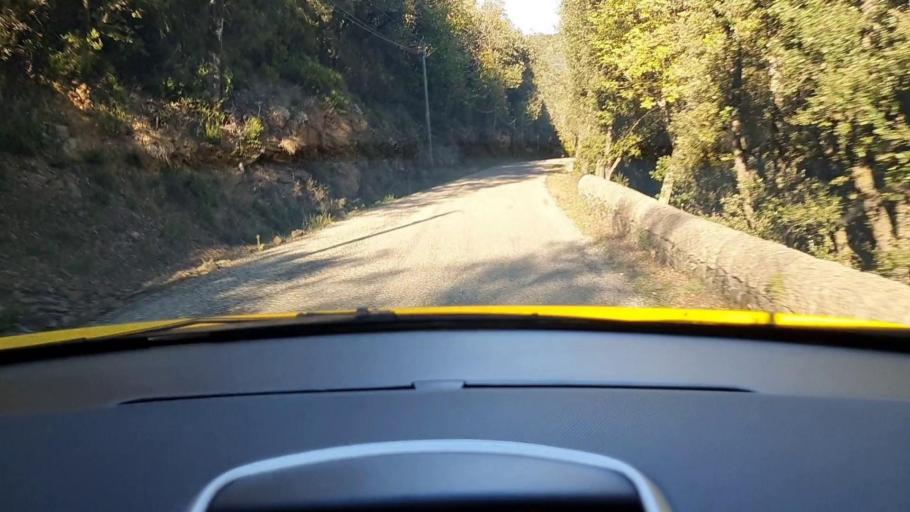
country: FR
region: Languedoc-Roussillon
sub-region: Departement du Gard
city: Sumene
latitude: 43.9839
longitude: 3.6821
